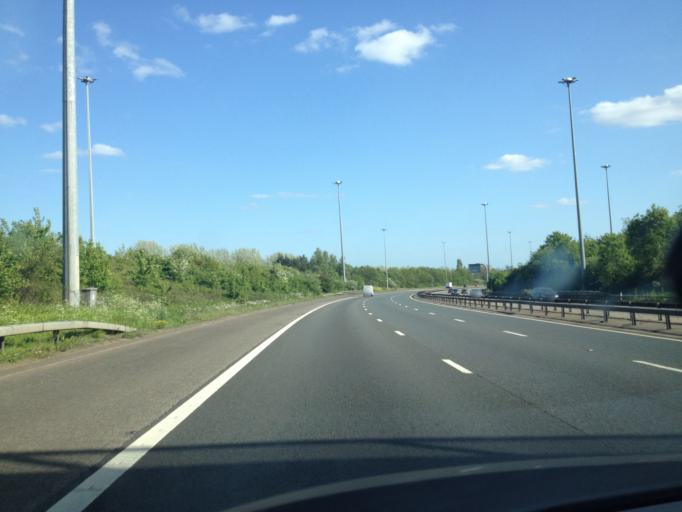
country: GB
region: England
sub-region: Hertfordshire
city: Borehamwood
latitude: 51.6348
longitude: -0.2654
